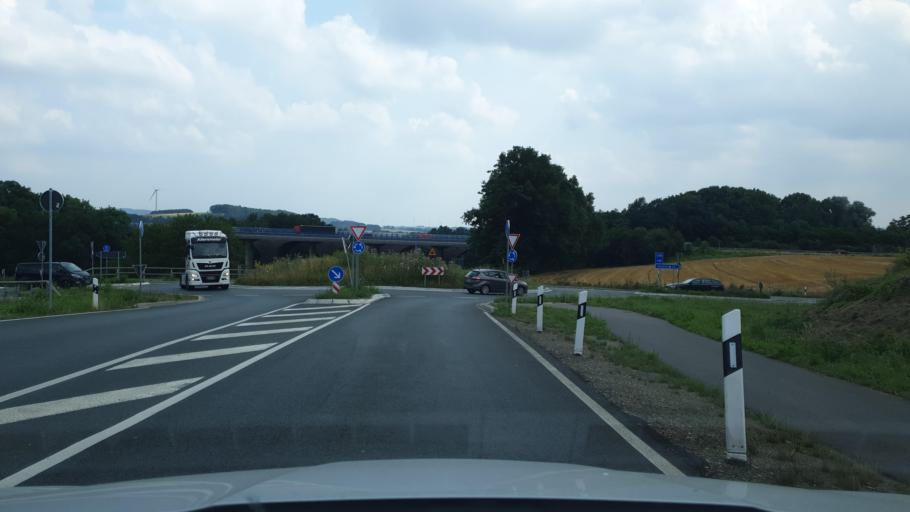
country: DE
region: North Rhine-Westphalia
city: Bad Oeynhausen
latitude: 52.1452
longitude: 8.7812
